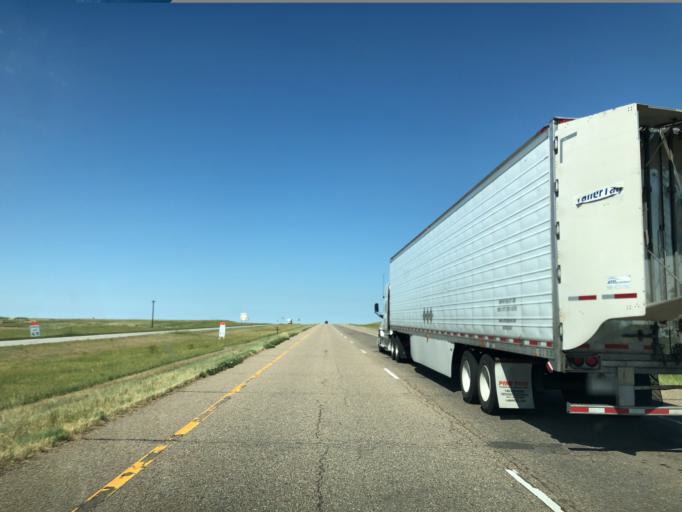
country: US
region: Colorado
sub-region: Lincoln County
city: Hugo
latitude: 39.2913
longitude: -102.8927
